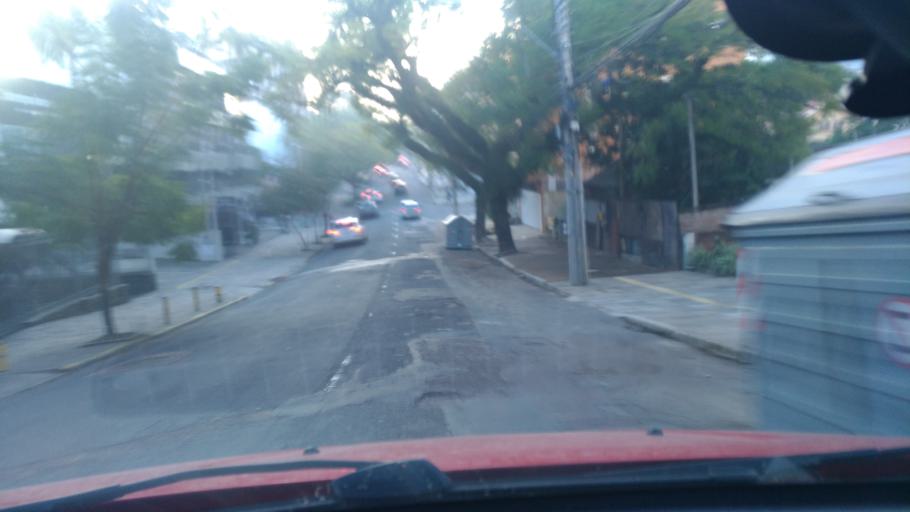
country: BR
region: Rio Grande do Sul
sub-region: Porto Alegre
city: Porto Alegre
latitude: -30.0271
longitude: -51.1924
